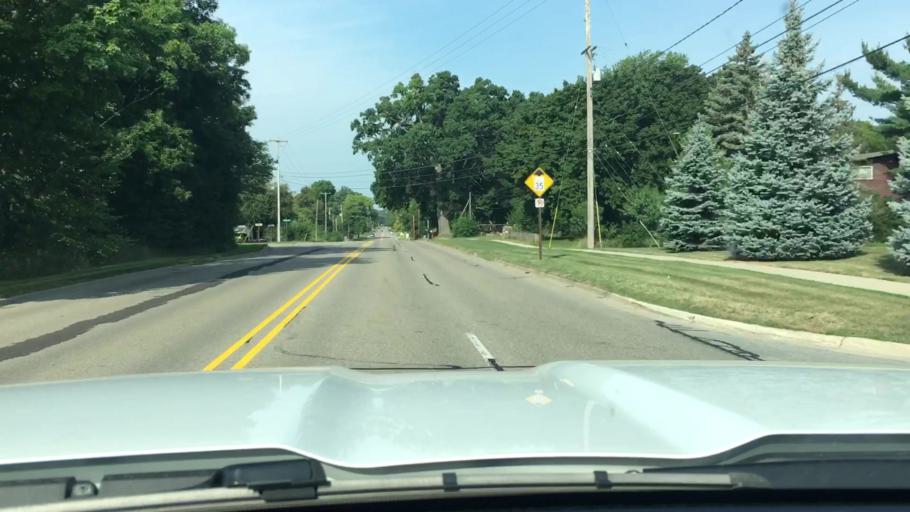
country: US
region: Michigan
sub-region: Kent County
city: Kentwood
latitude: 42.8409
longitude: -85.6316
